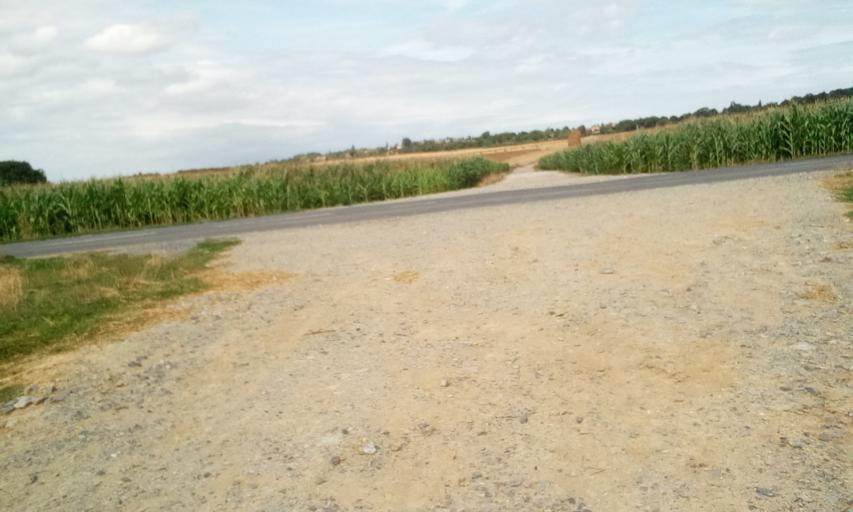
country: FR
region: Lower Normandy
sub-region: Departement du Calvados
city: Herouvillette
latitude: 49.2269
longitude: -0.2364
